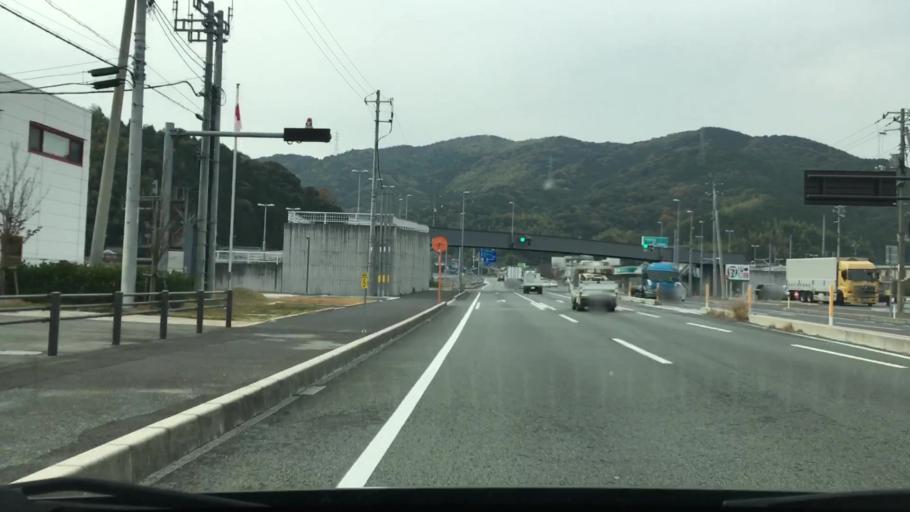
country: JP
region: Yamaguchi
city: Hofu
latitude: 34.0756
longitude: 131.6880
